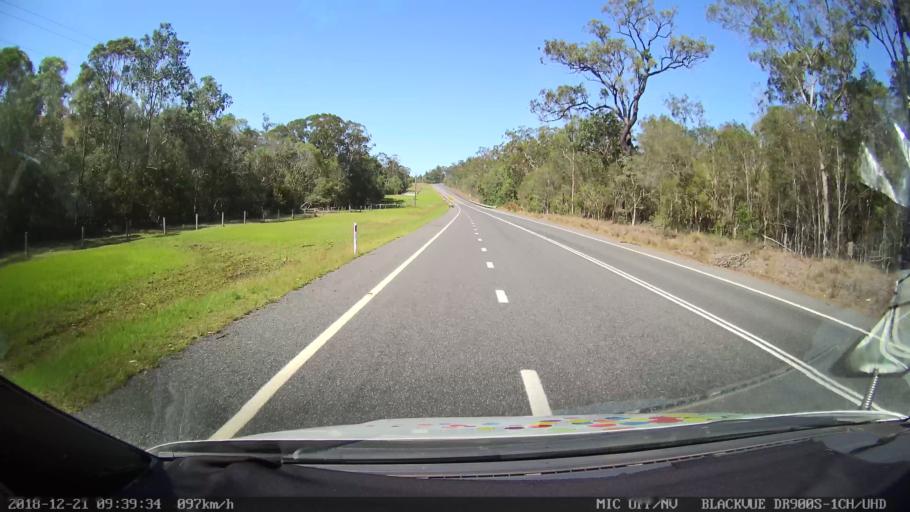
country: AU
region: New South Wales
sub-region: Clarence Valley
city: Grafton
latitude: -29.5624
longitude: 152.9712
